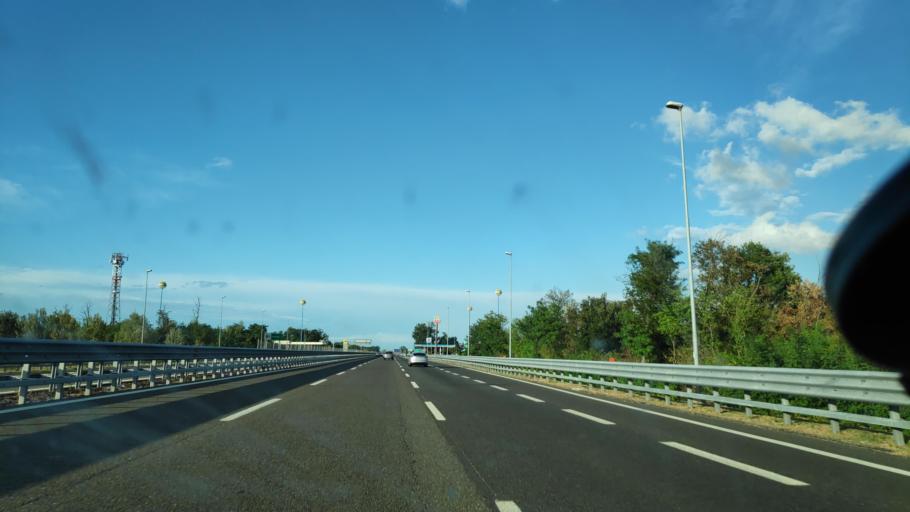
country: IT
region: Piedmont
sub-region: Provincia di Alessandria
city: Tortona
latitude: 44.9313
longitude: 8.8510
